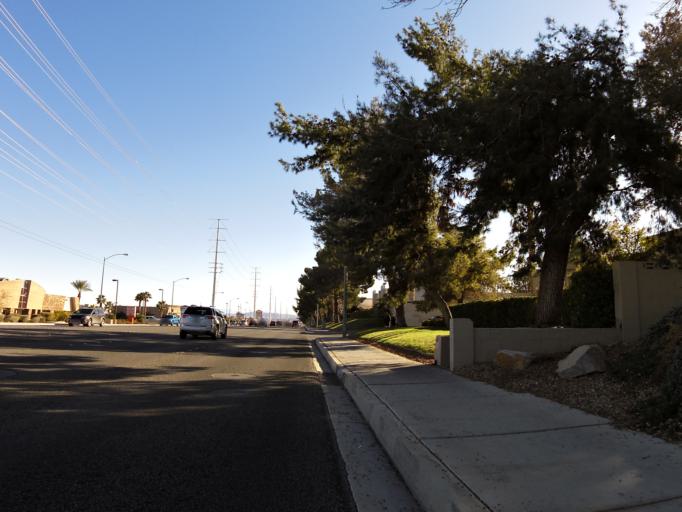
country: US
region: Nevada
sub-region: Clark County
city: Spring Valley
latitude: 36.1353
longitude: -115.2789
